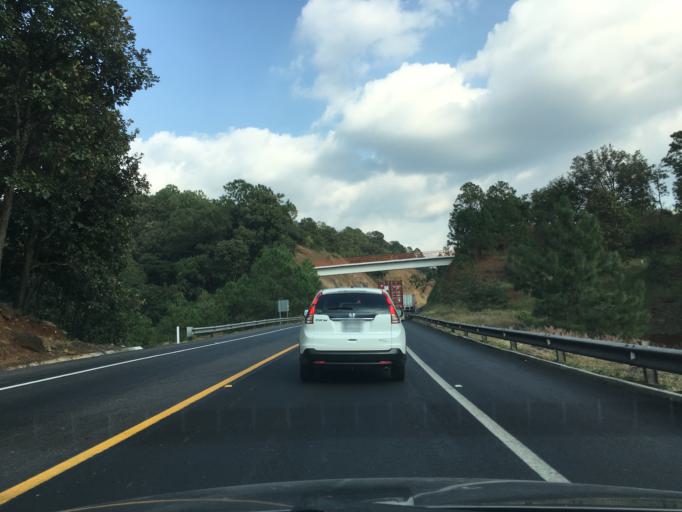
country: MX
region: Michoacan
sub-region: Ziracuaretiro
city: Patuan
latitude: 19.4341
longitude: -101.9063
